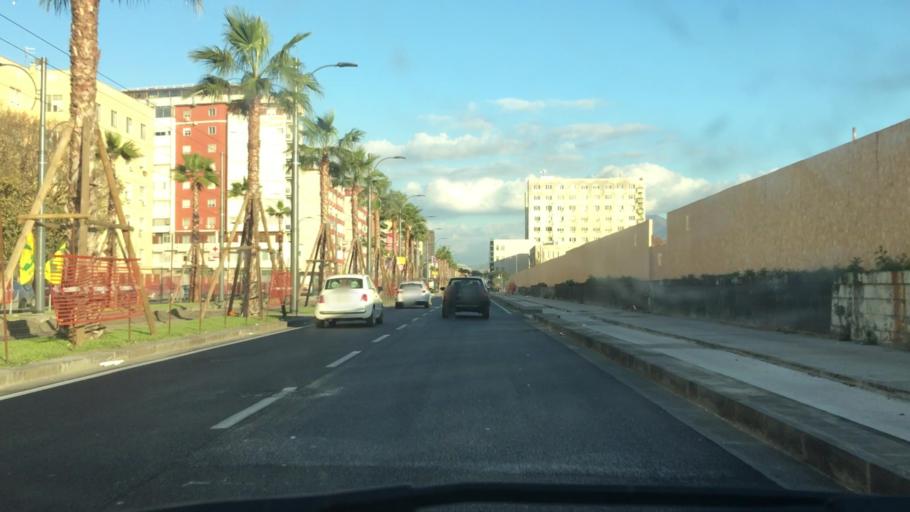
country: IT
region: Campania
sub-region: Provincia di Napoli
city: Napoli
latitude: 40.8464
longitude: 14.2711
